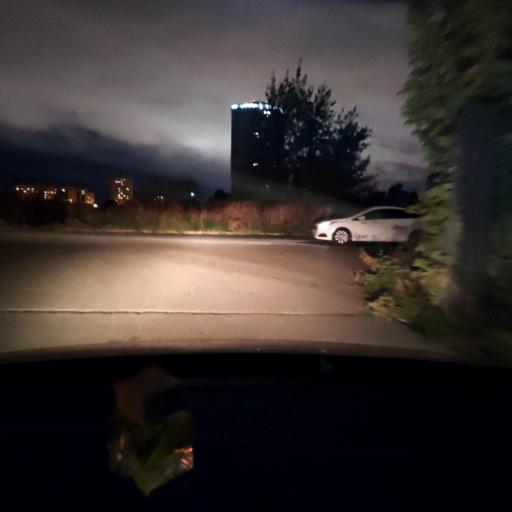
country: RU
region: Tatarstan
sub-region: Gorod Kazan'
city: Kazan
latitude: 55.7926
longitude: 49.1934
